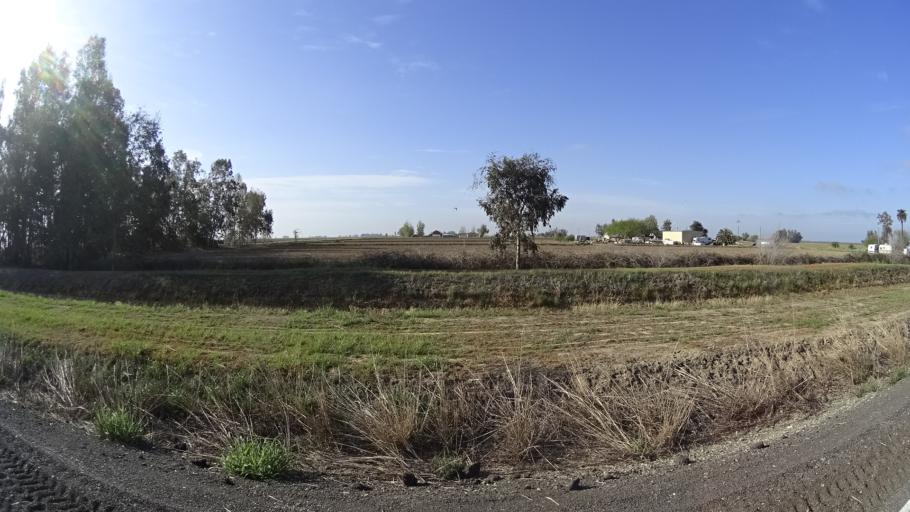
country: US
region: California
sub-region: Glenn County
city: Willows
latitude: 39.5820
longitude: -122.1057
